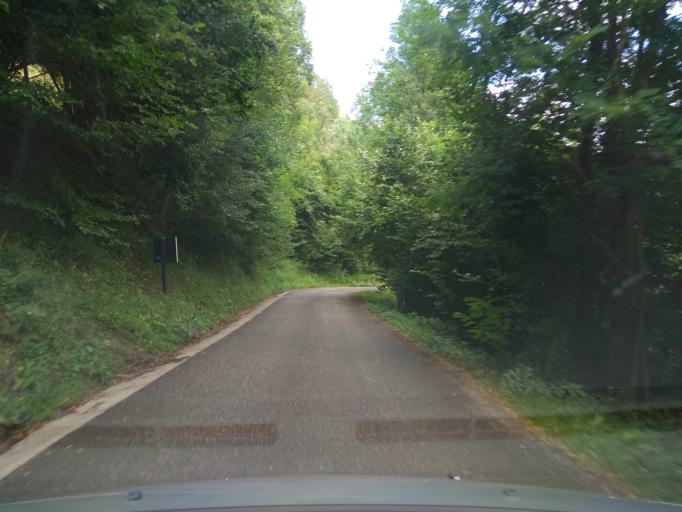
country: ES
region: Catalonia
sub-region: Provincia de Lleida
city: Vielha
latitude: 42.6994
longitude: 0.7097
